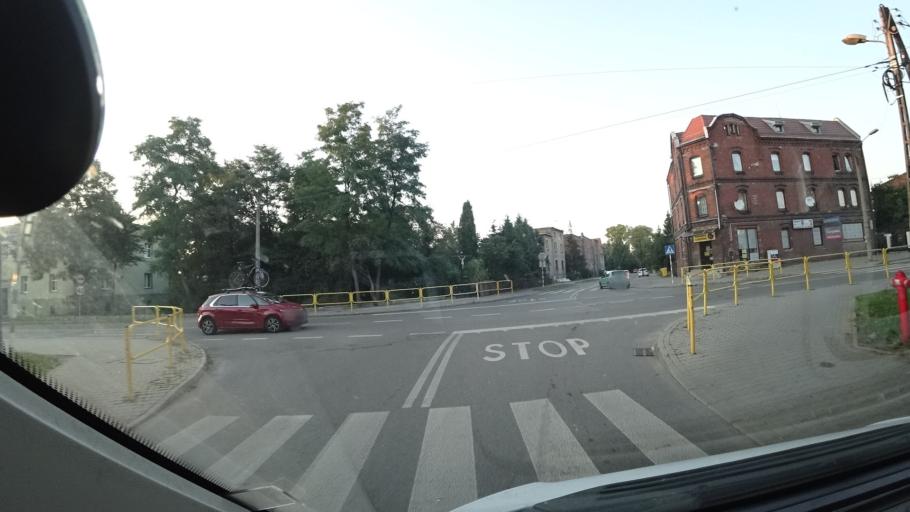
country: PL
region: Silesian Voivodeship
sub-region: Ruda Slaska
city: Ruda Slaska
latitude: 50.2809
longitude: 18.8159
